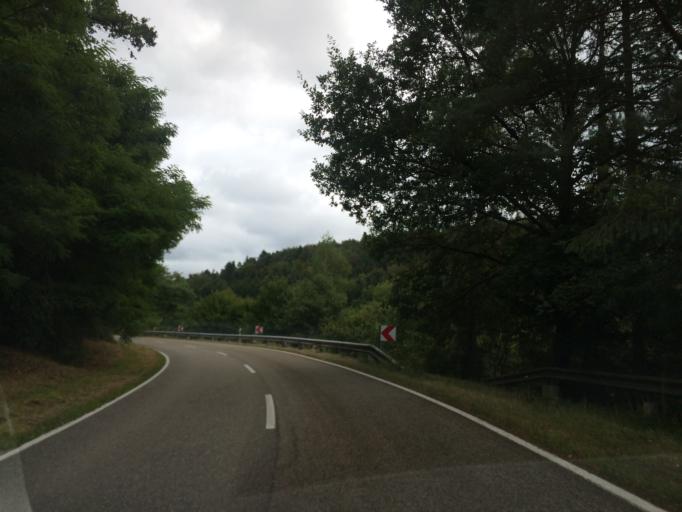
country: DE
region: Rheinland-Pfalz
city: Bundenthal
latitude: 49.0915
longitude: 7.8135
